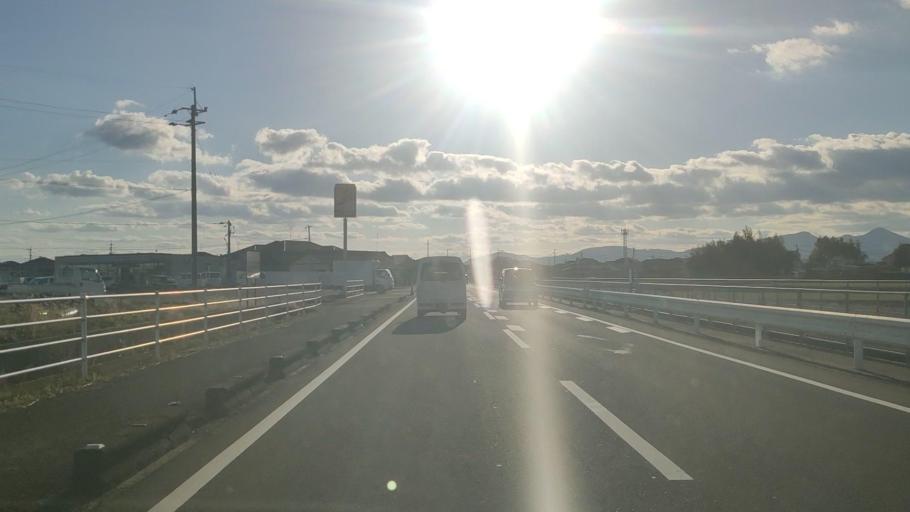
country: JP
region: Saga Prefecture
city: Saga-shi
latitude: 33.2823
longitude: 130.2297
